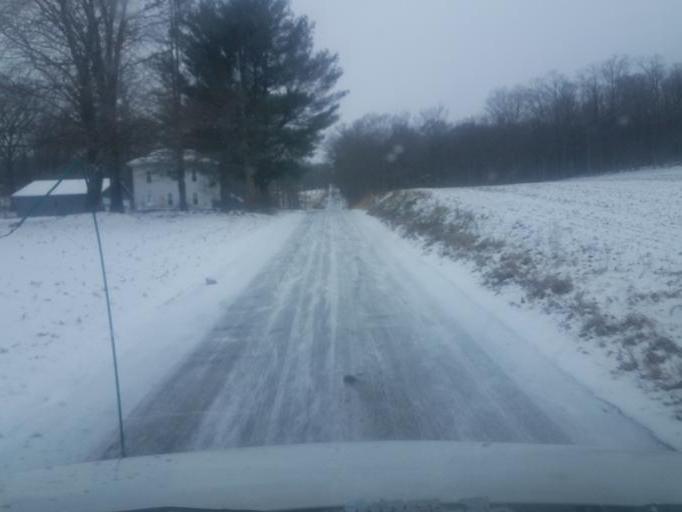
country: US
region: Ohio
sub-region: Sandusky County
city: Bellville
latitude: 40.6055
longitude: -82.4162
